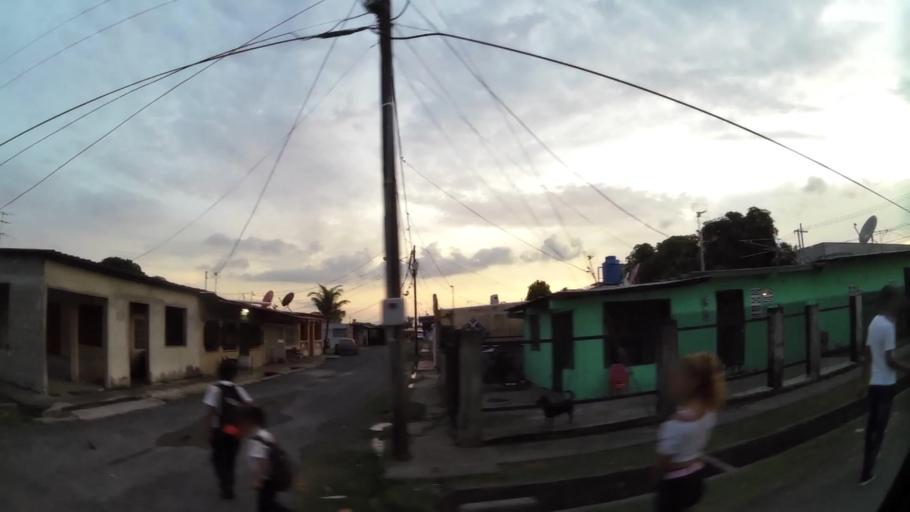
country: PA
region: Panama
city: Tocumen
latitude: 9.0804
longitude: -79.3985
